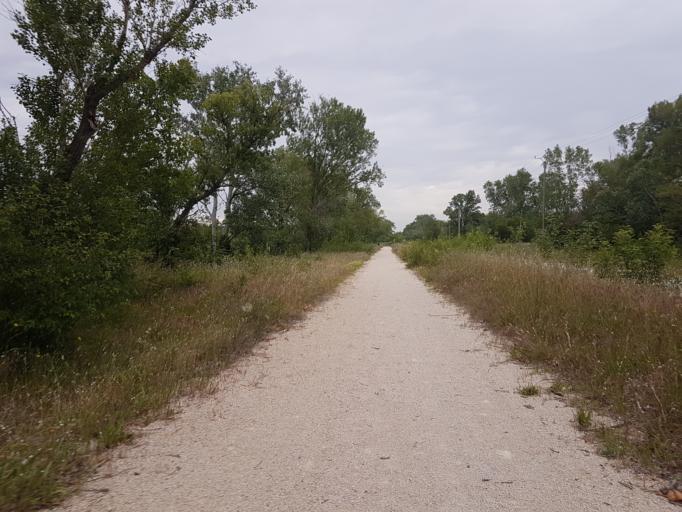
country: FR
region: Languedoc-Roussillon
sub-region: Departement du Gard
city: Roquemaure
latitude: 44.0671
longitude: 4.7761
